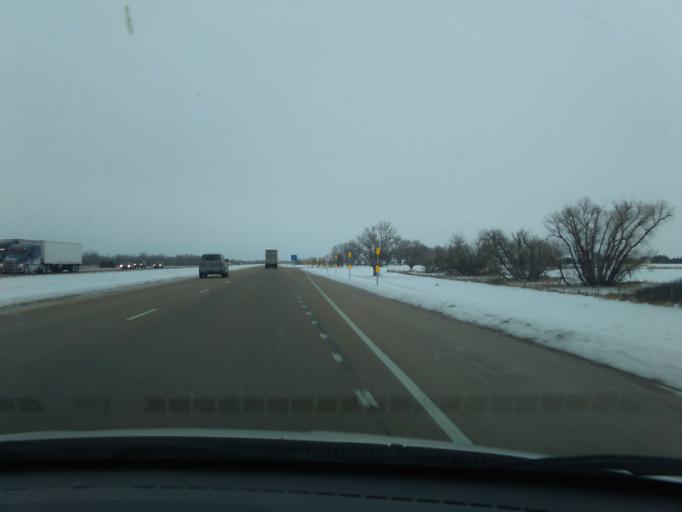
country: US
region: Nebraska
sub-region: Keith County
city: Ogallala
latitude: 41.1059
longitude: -101.7623
